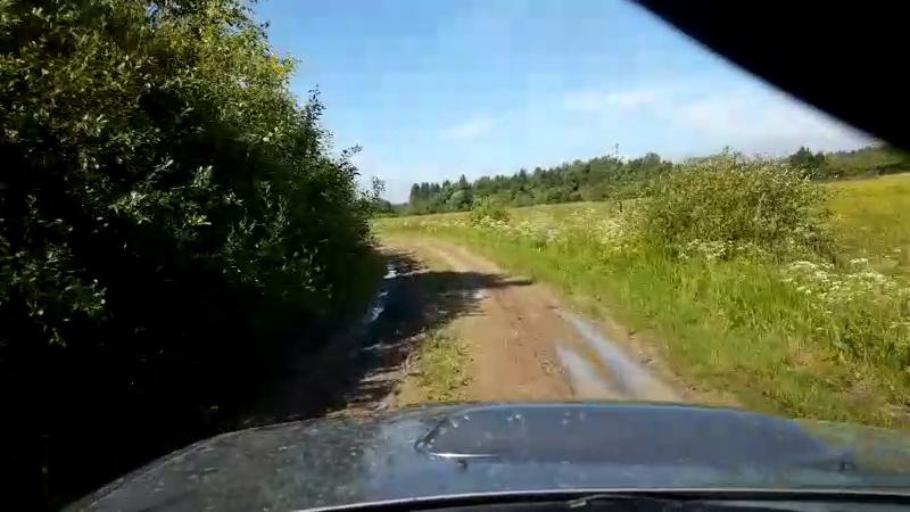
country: EE
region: Paernumaa
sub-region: Sindi linn
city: Sindi
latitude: 58.5080
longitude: 24.6474
